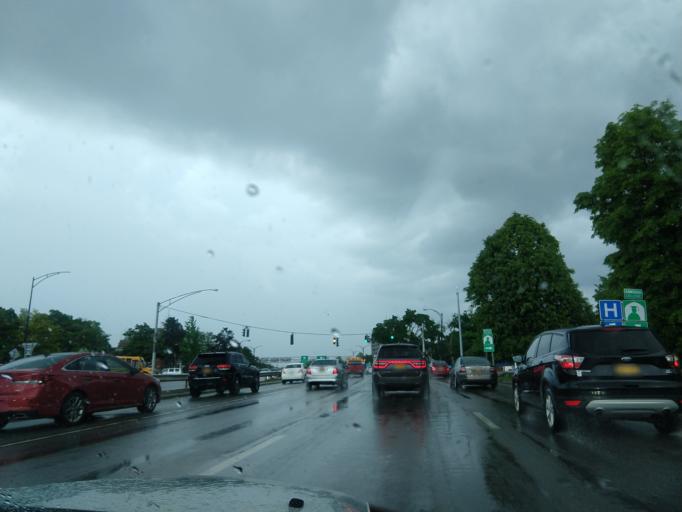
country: US
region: New York
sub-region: Erie County
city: Kenmore
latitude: 42.9307
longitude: -78.8555
